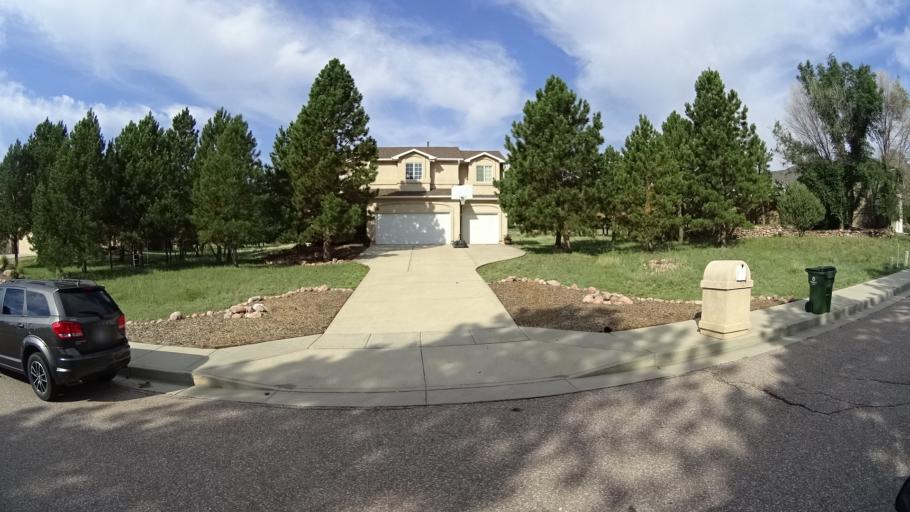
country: US
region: Colorado
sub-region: El Paso County
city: Air Force Academy
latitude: 38.9408
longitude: -104.8234
